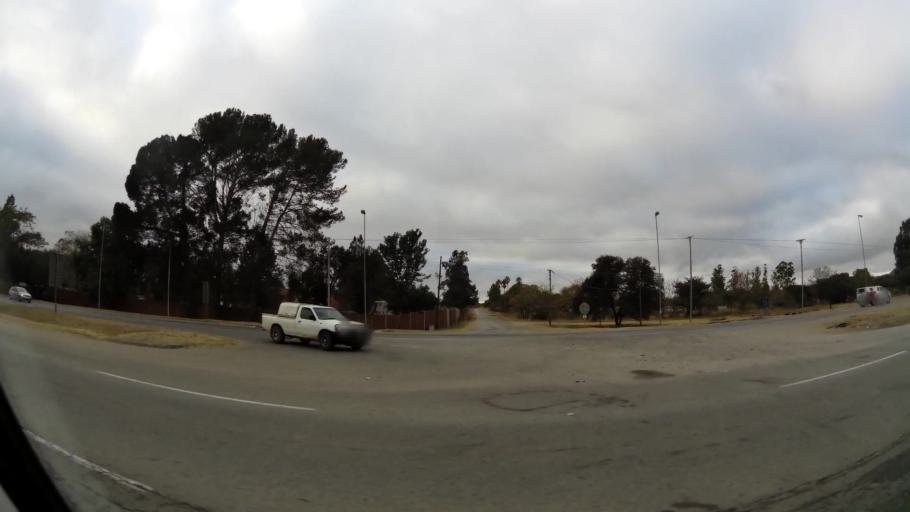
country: ZA
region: Limpopo
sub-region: Capricorn District Municipality
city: Polokwane
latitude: -23.9292
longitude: 29.4272
